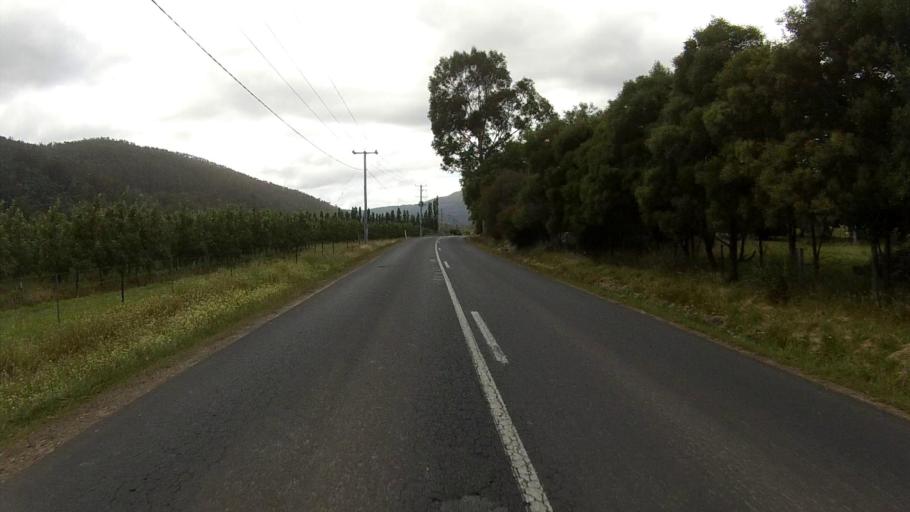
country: AU
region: Tasmania
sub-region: Huon Valley
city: Cygnet
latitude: -43.1672
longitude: 147.1218
